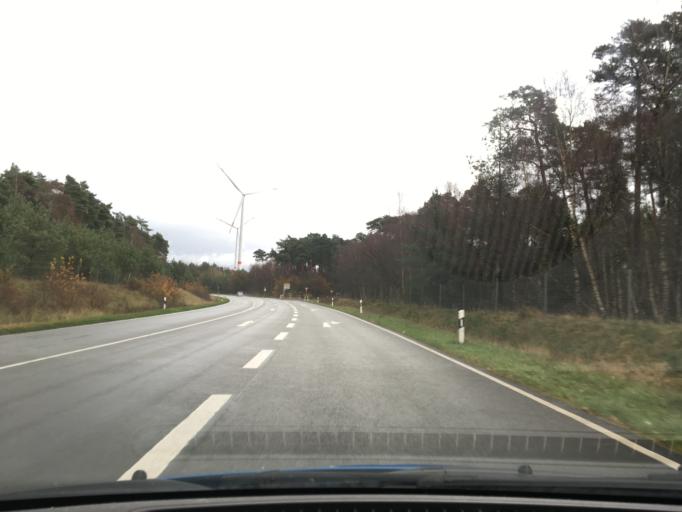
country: DE
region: Lower Saxony
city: Embsen
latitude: 53.1927
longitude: 10.3692
